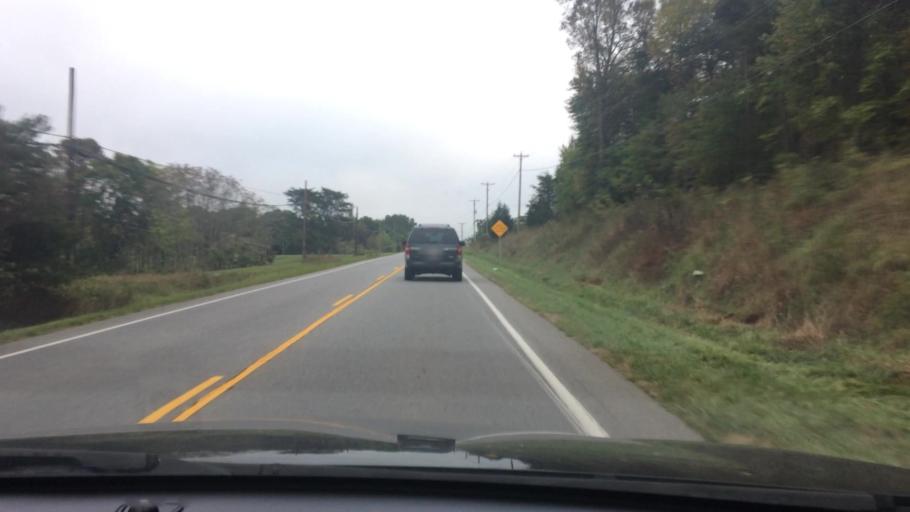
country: US
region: Virginia
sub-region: Franklin County
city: Rocky Mount
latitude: 37.0178
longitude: -79.8371
